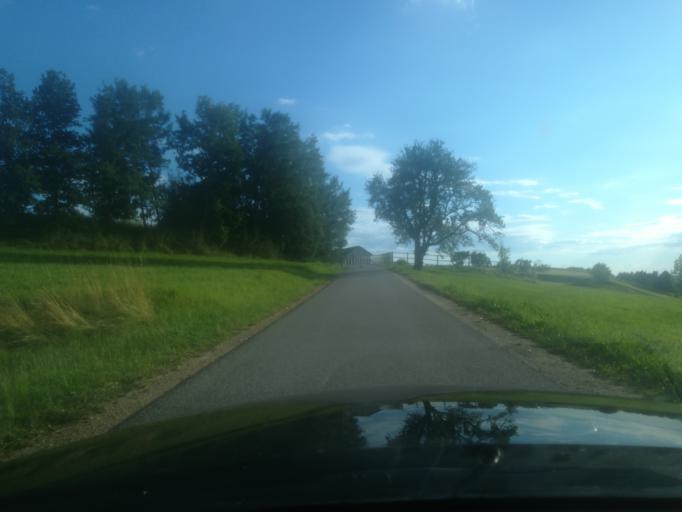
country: AT
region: Upper Austria
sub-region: Politischer Bezirk Perg
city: Perg
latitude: 48.3535
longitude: 14.5714
